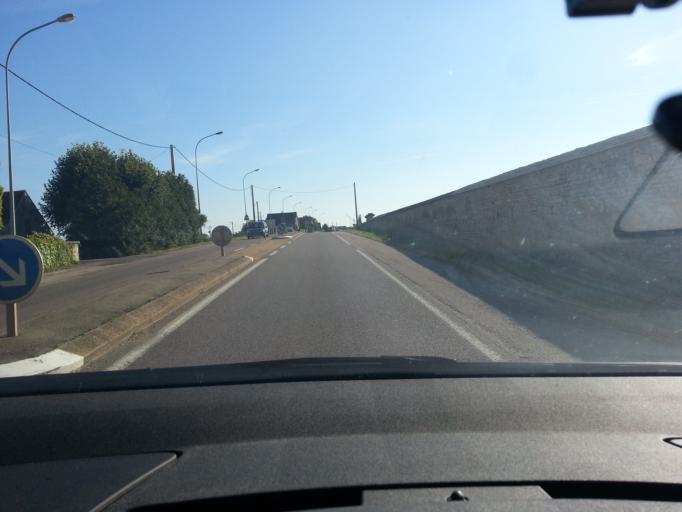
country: FR
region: Bourgogne
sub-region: Departement de la Cote-d'Or
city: Nuits-Saint-Georges
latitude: 47.1084
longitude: 4.9281
